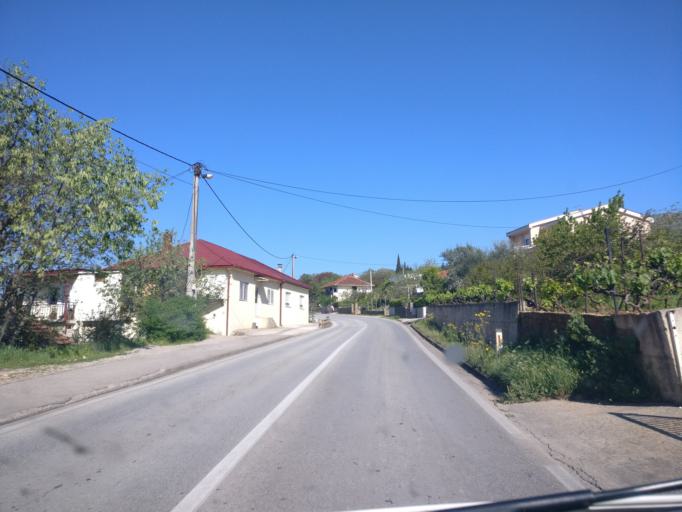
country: BA
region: Federation of Bosnia and Herzegovina
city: Capljina
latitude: 43.1403
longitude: 17.6666
